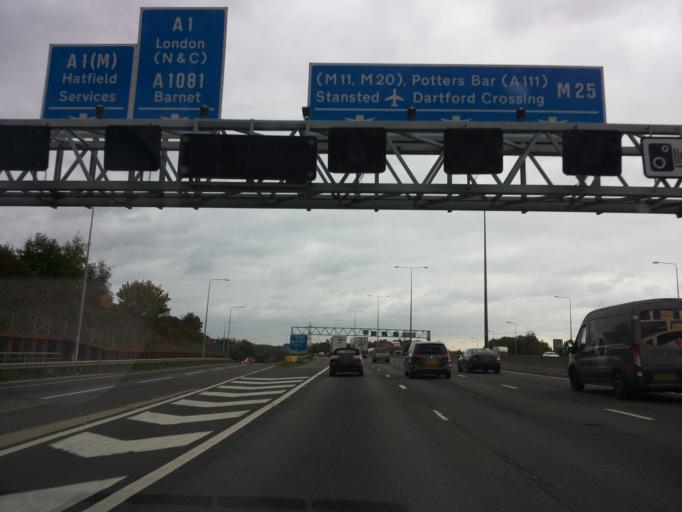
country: GB
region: England
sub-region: Greater London
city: High Barnet
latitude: 51.6896
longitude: -0.2339
